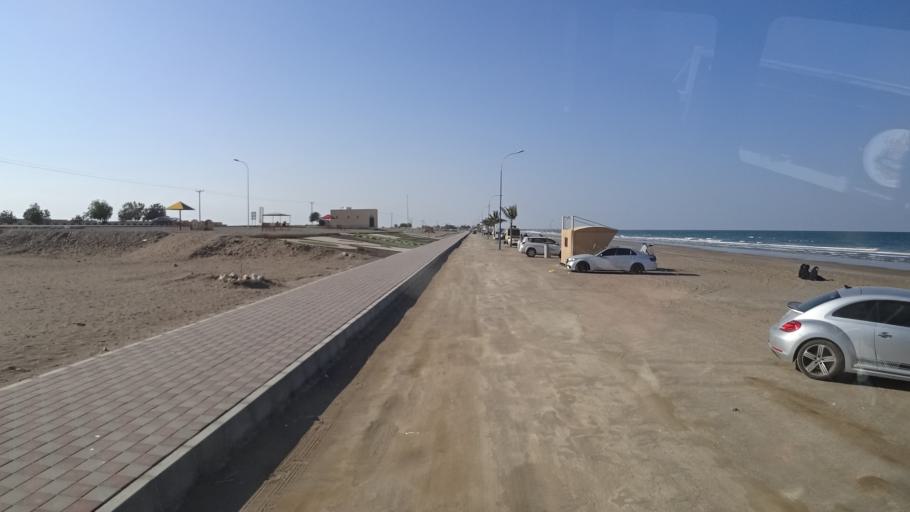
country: OM
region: Al Batinah
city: Al Khaburah
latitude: 23.9582
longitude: 57.1379
